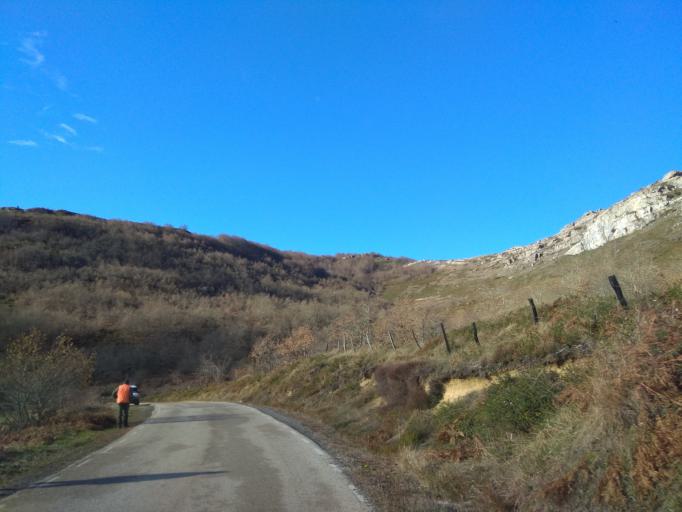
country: ES
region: Cantabria
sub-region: Provincia de Cantabria
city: San Martin de Elines
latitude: 42.9357
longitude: -3.8322
